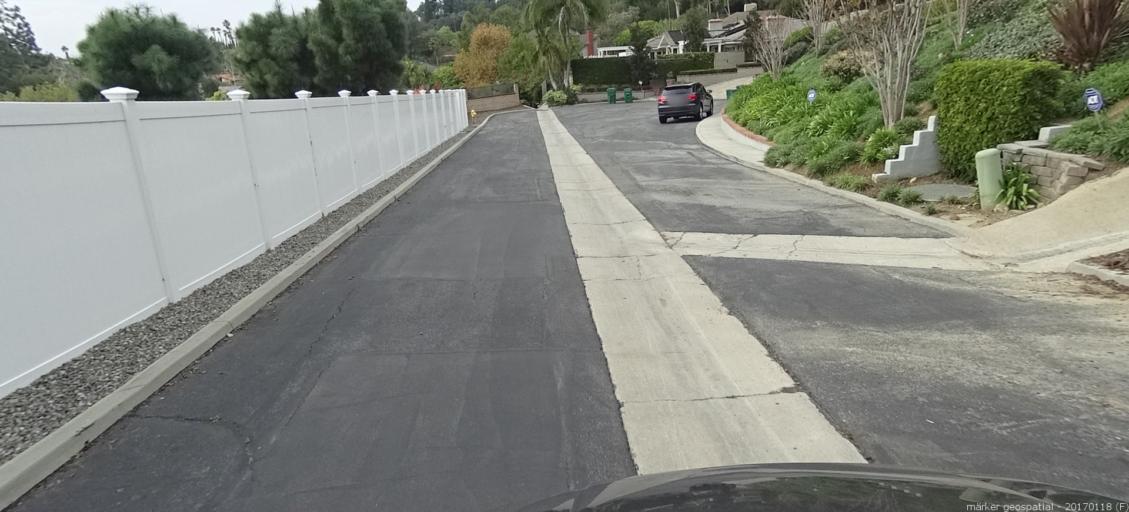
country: US
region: California
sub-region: Orange County
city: North Tustin
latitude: 33.7552
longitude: -117.7791
